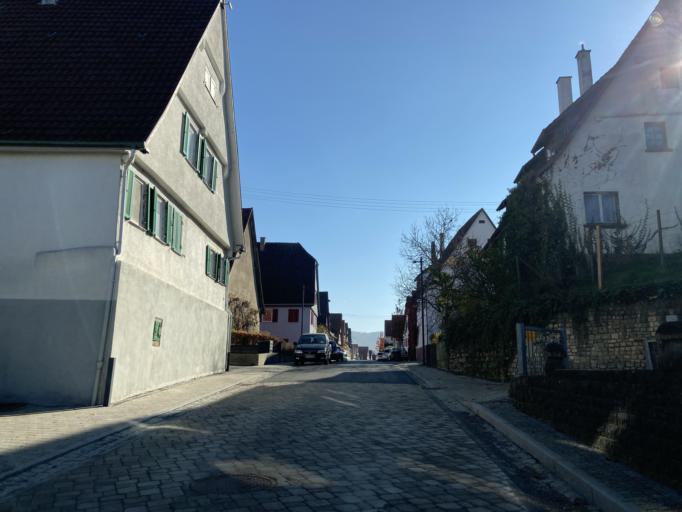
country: DE
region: Baden-Wuerttemberg
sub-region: Tuebingen Region
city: Nehren
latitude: 48.4343
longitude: 9.0657
